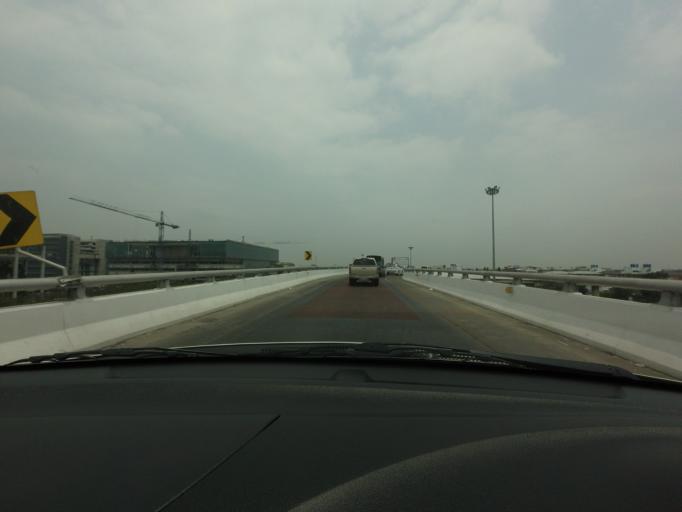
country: TH
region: Bangkok
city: Thawi Watthana
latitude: 13.7887
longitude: 100.3277
